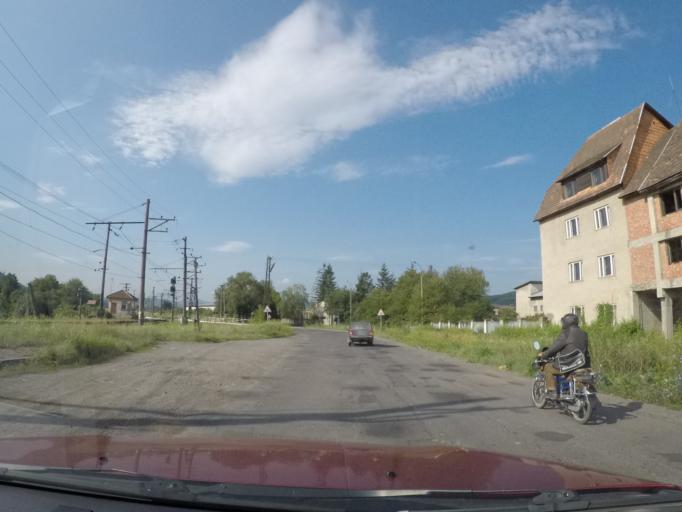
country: UA
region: Zakarpattia
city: Velykyi Bereznyi
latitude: 48.9086
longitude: 22.4586
